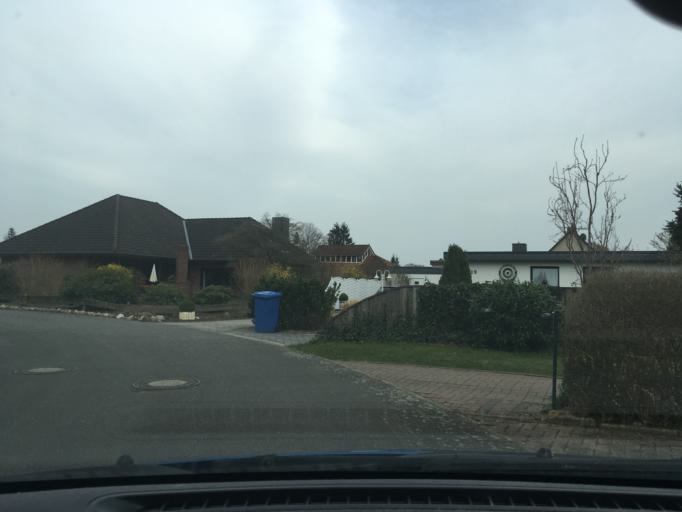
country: DE
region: Lower Saxony
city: Tespe
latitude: 53.3906
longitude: 10.4191
